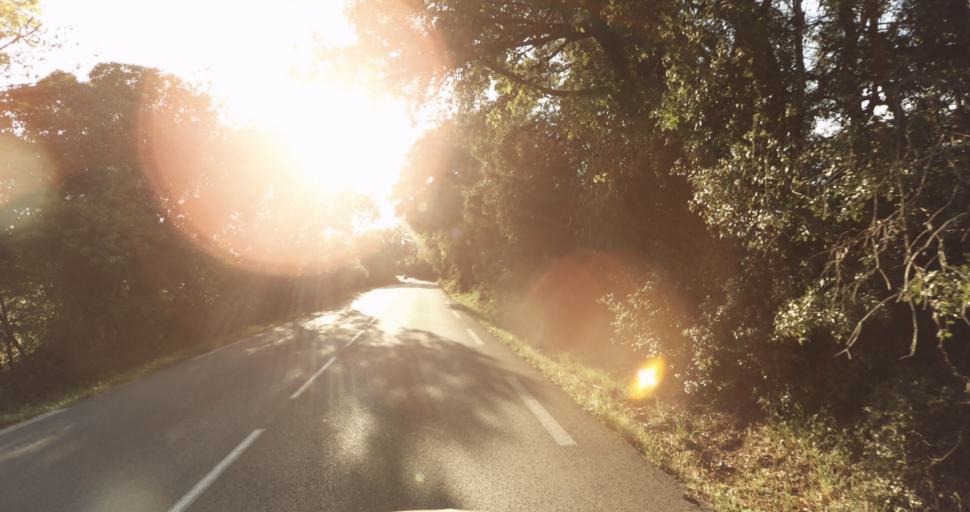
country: FR
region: Provence-Alpes-Cote d'Azur
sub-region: Departement du Var
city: Hyeres
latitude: 43.1515
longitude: 6.1443
